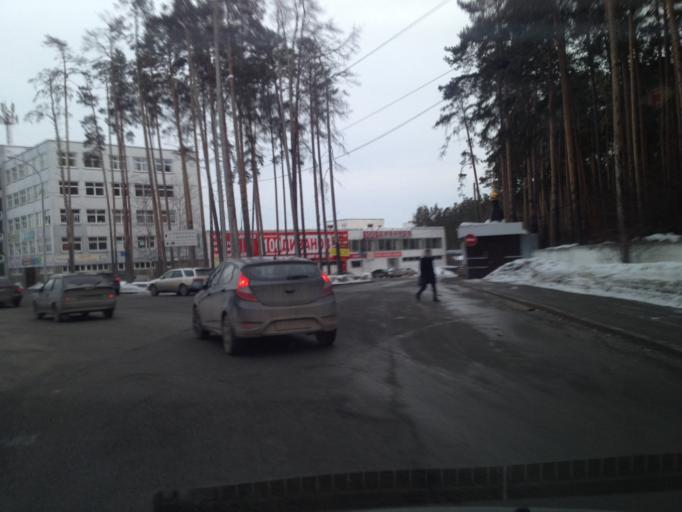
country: RU
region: Sverdlovsk
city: Shirokaya Rechka
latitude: 56.8147
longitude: 60.5346
